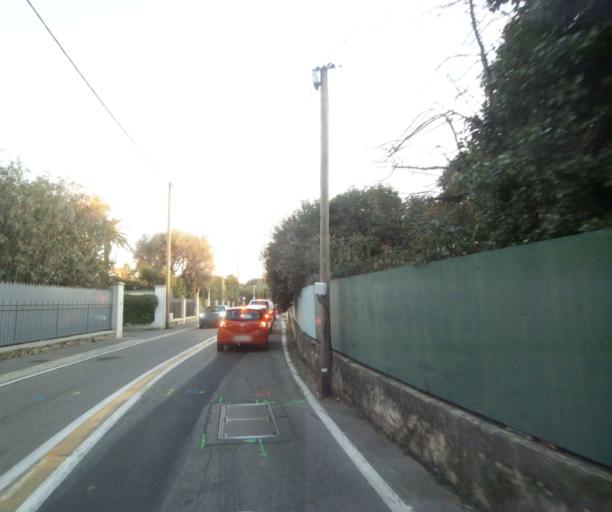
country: FR
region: Provence-Alpes-Cote d'Azur
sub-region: Departement des Alpes-Maritimes
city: Antibes
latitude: 43.5578
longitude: 7.1285
